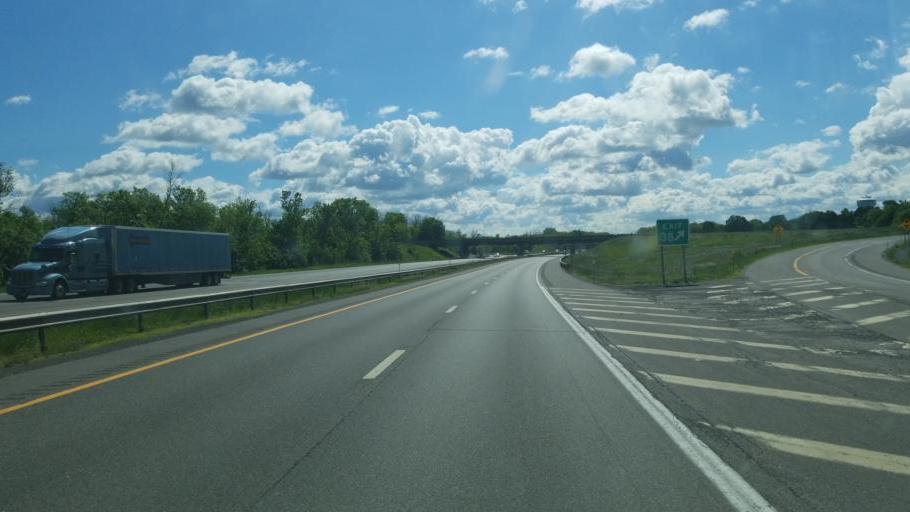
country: US
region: New York
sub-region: Onondaga County
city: Liverpool
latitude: 43.1176
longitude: -76.2216
